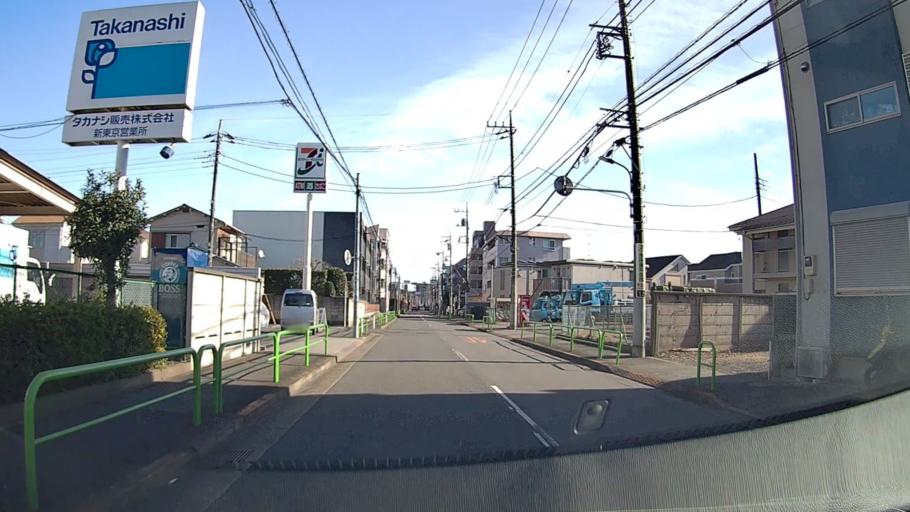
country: JP
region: Saitama
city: Wako
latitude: 35.7531
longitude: 139.6128
